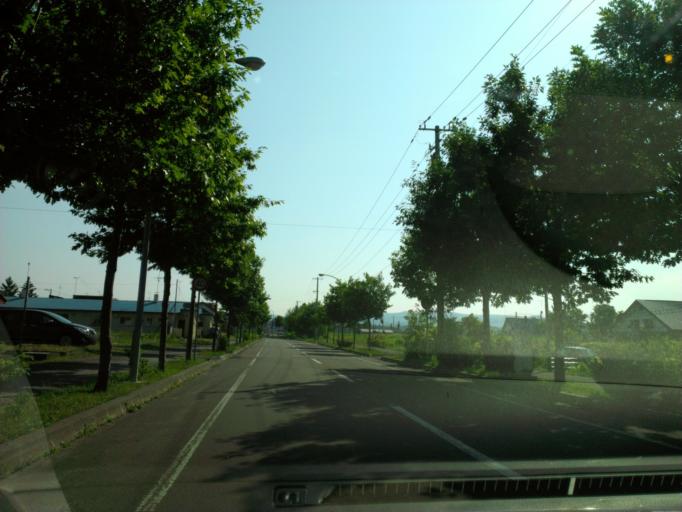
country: JP
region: Hokkaido
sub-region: Asahikawa-shi
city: Asahikawa
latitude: 43.5970
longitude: 142.4705
